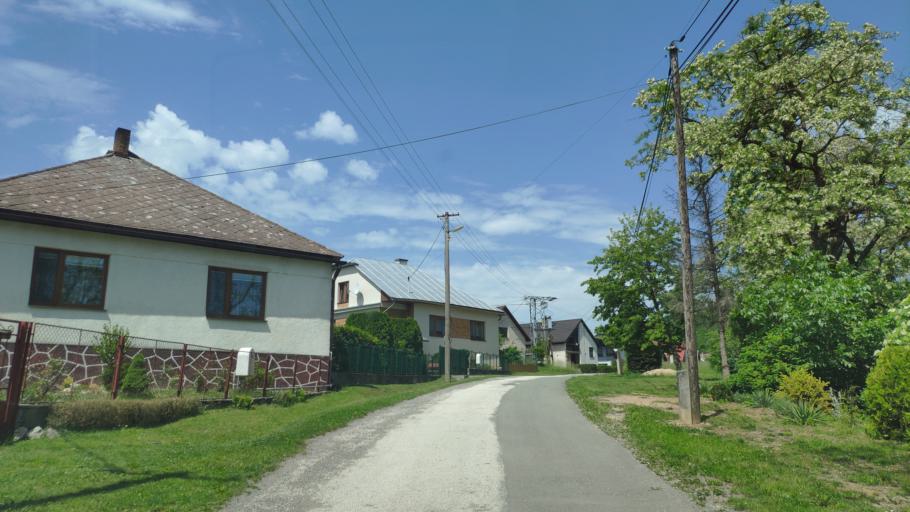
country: SK
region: Kosicky
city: Medzev
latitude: 48.7165
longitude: 20.9719
